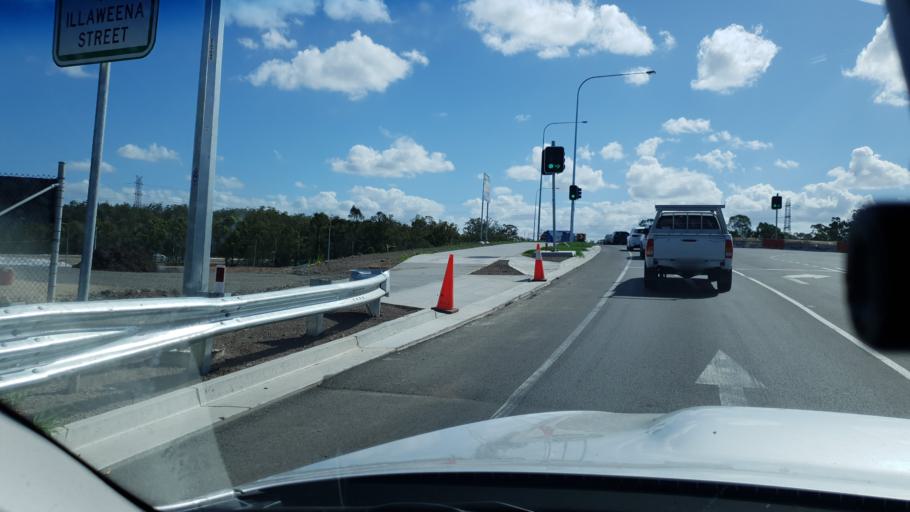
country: AU
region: Queensland
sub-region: Logan
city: Woodridge
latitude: -27.6515
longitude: 153.0713
